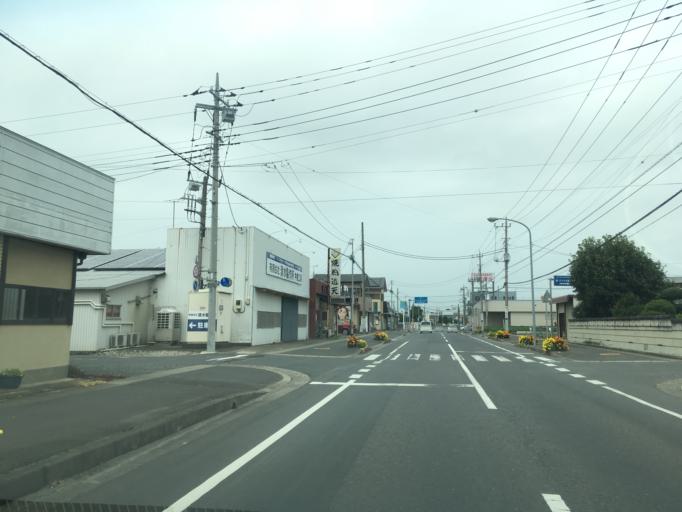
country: JP
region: Ibaraki
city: Katsuta
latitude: 36.3864
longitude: 140.5455
